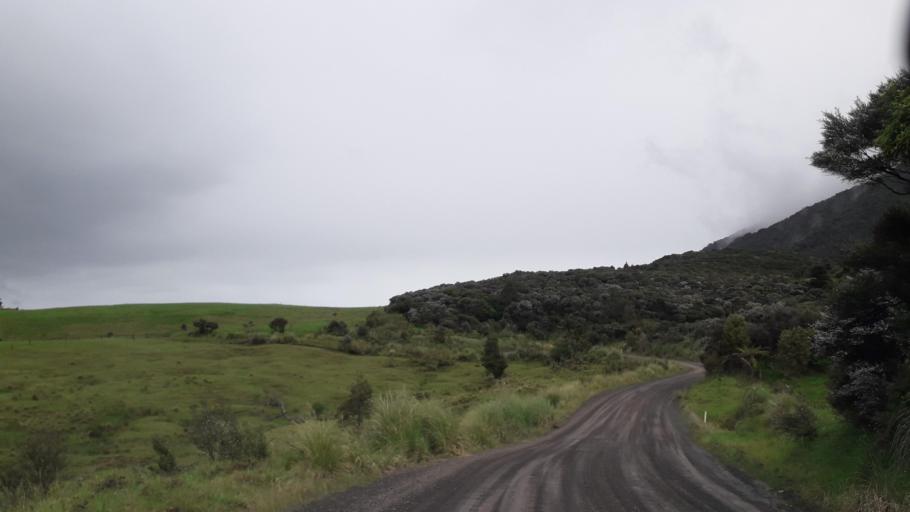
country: NZ
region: Northland
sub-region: Far North District
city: Kaitaia
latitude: -35.4067
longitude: 173.3647
